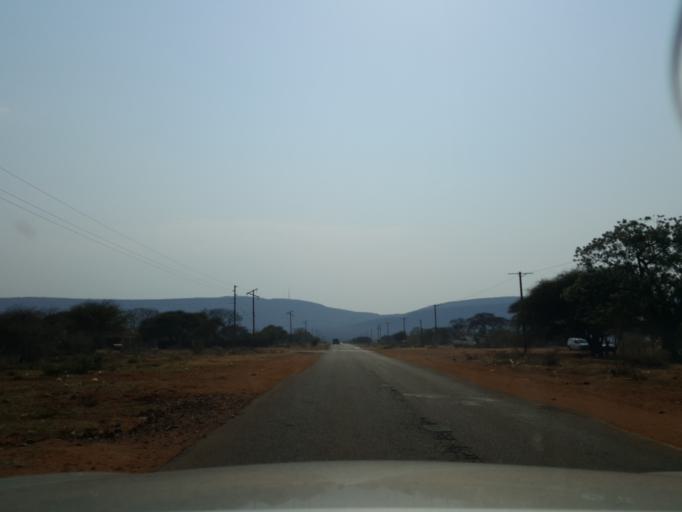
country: BW
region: South East
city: Lobatse
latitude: -25.2996
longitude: 25.8348
